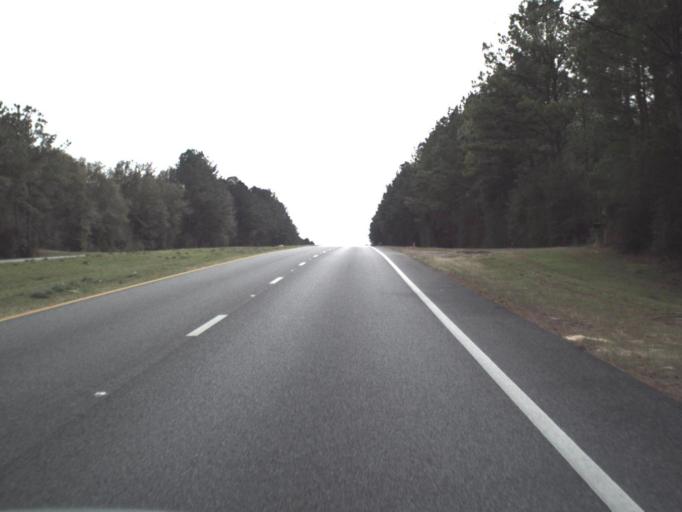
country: US
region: Florida
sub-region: Bay County
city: Youngstown
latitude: 30.5573
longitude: -85.3897
